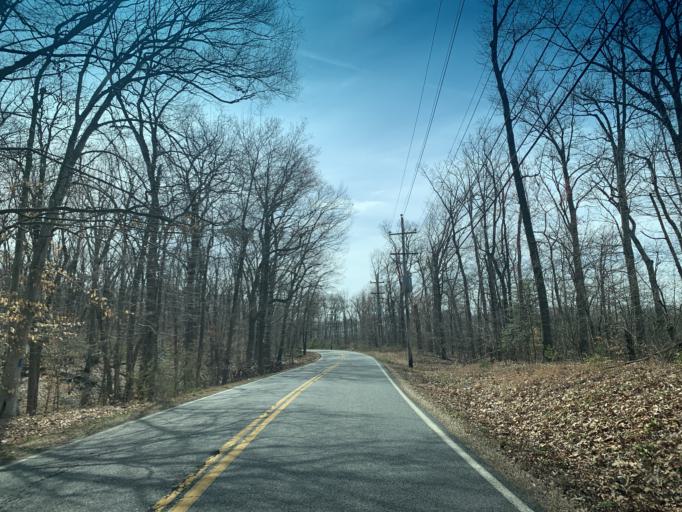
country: US
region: Maryland
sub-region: Cecil County
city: Charlestown
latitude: 39.5679
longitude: -76.0229
